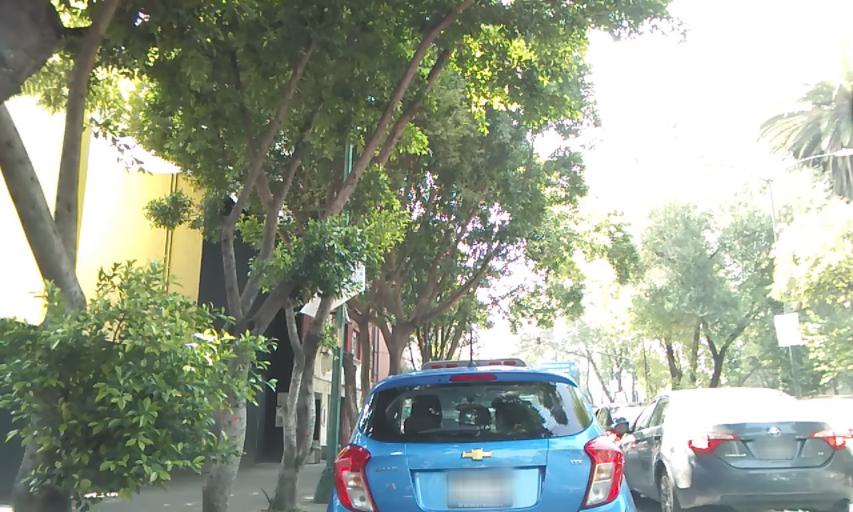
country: MX
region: Mexico City
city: Cuauhtemoc
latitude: 19.4333
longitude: -99.1614
